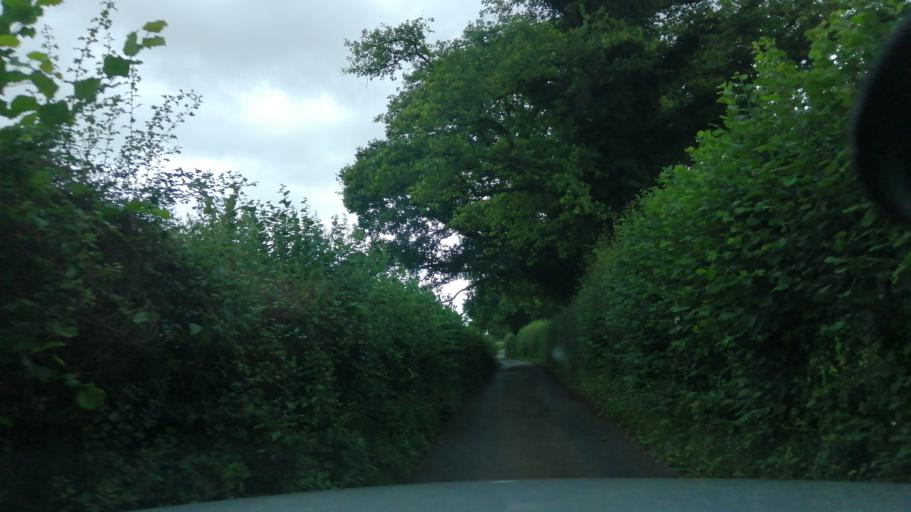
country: GB
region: England
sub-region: Herefordshire
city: Madley
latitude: 52.0206
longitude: -2.8649
